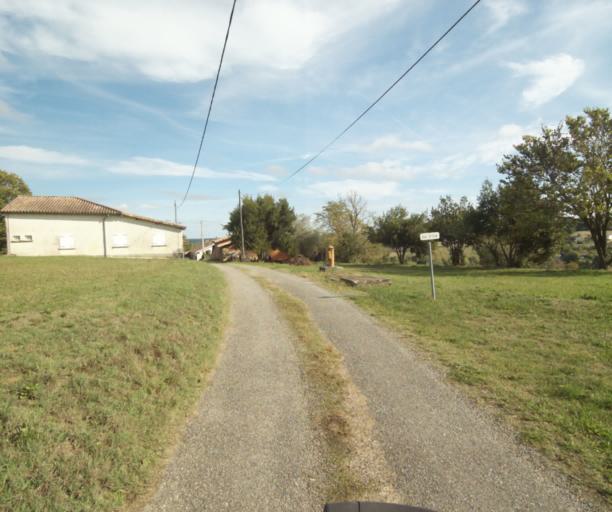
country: FR
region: Midi-Pyrenees
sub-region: Departement du Tarn-et-Garonne
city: Saint-Porquier
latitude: 43.9452
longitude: 1.1673
